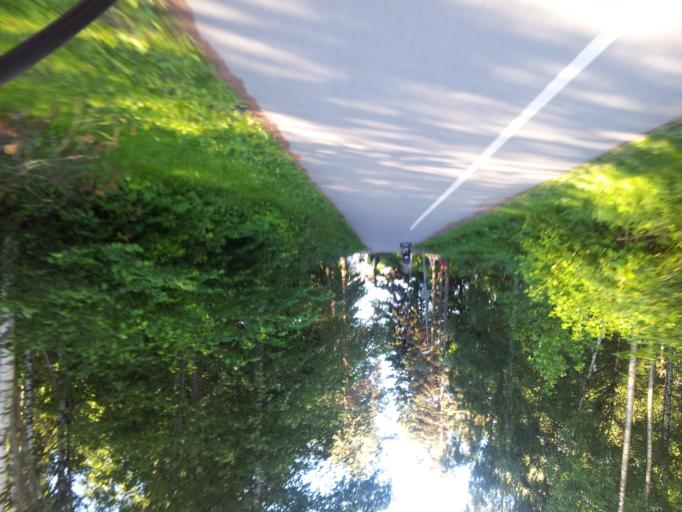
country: SE
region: Uppsala
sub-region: Uppsala Kommun
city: Gamla Uppsala
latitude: 59.8797
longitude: 17.6271
